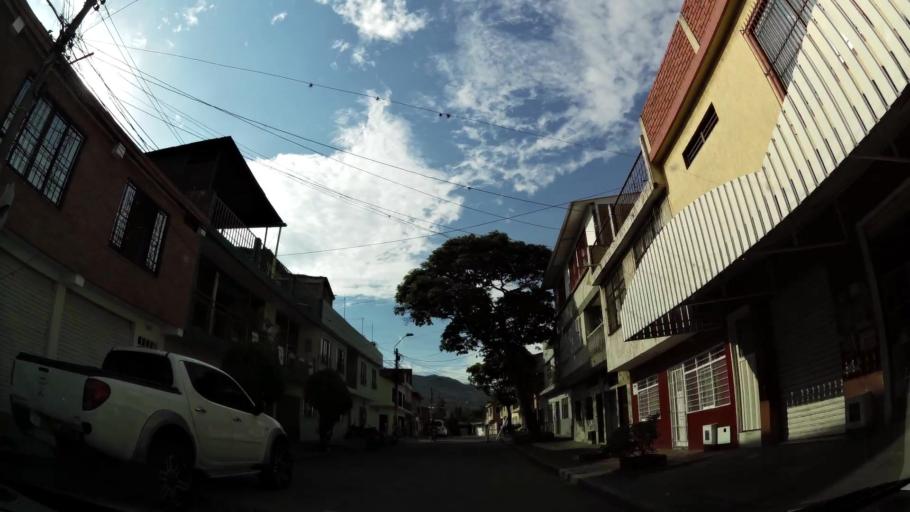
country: CO
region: Valle del Cauca
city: Cali
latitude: 3.4731
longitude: -76.5133
